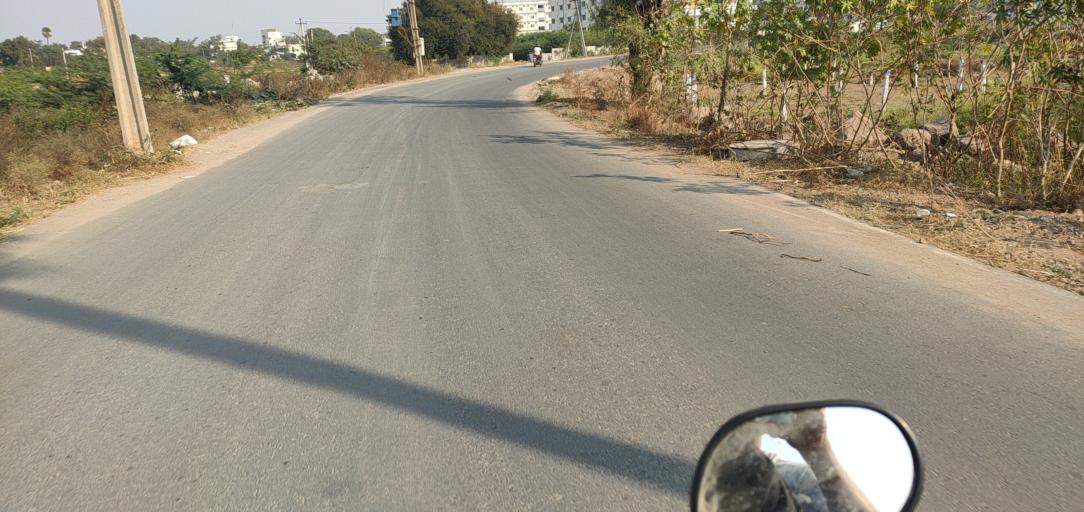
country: IN
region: Telangana
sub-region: Rangareddi
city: Lal Bahadur Nagar
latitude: 17.3421
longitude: 78.6215
